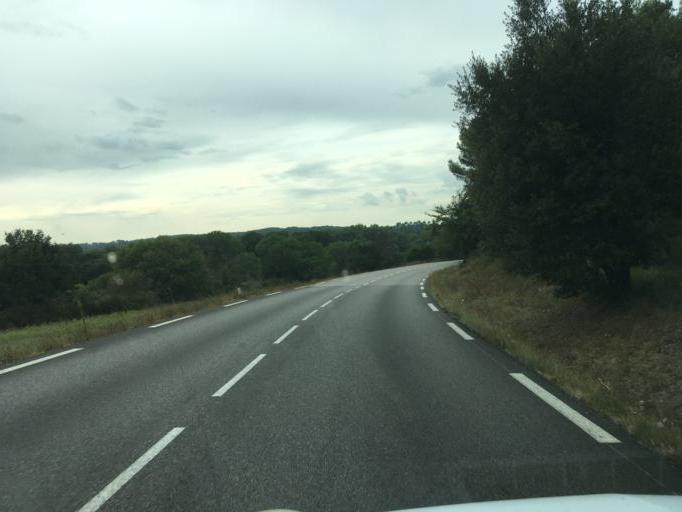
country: FR
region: Provence-Alpes-Cote d'Azur
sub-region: Departement des Bouches-du-Rhone
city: Meyreuil
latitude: 43.4880
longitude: 5.5278
